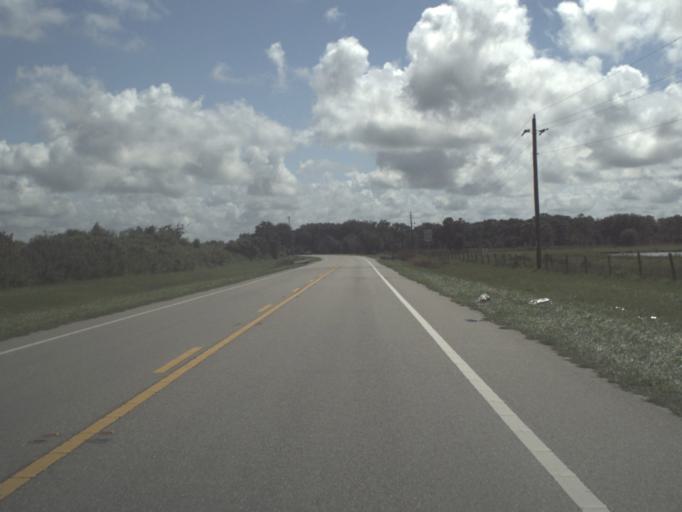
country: US
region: Florida
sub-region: Sarasota County
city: Lake Sarasota
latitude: 27.3645
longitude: -82.2051
